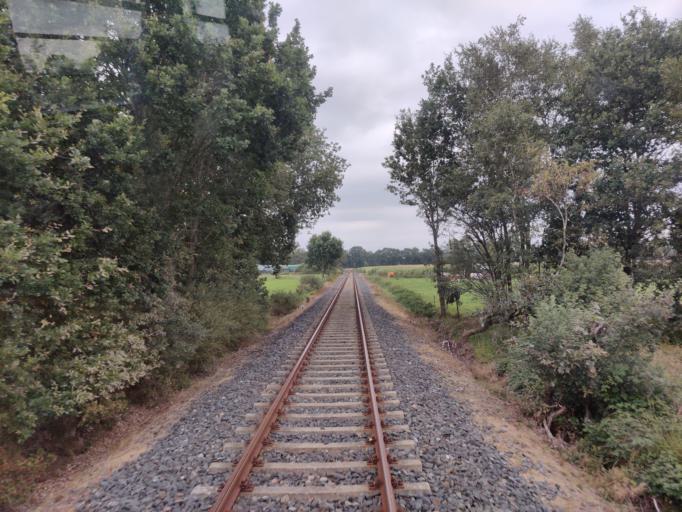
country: DE
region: Lower Saxony
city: Vollersode
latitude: 53.2893
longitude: 8.9701
